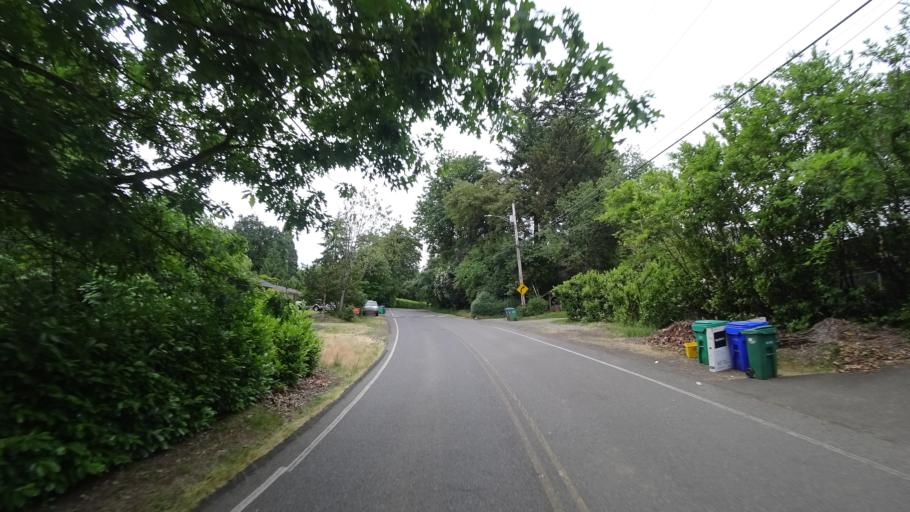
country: US
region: Oregon
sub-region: Clackamas County
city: Lake Oswego
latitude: 45.4608
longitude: -122.6828
